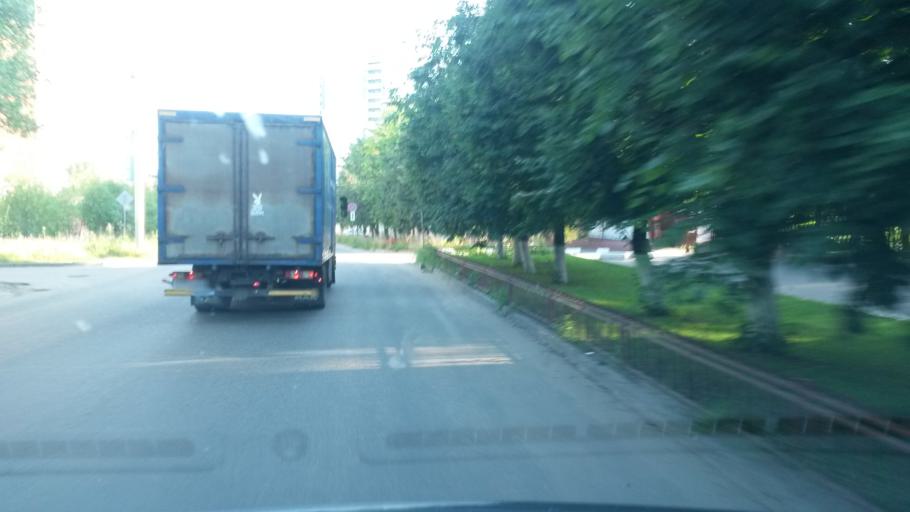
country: RU
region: Ivanovo
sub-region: Gorod Ivanovo
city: Ivanovo
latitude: 57.0006
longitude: 40.9428
